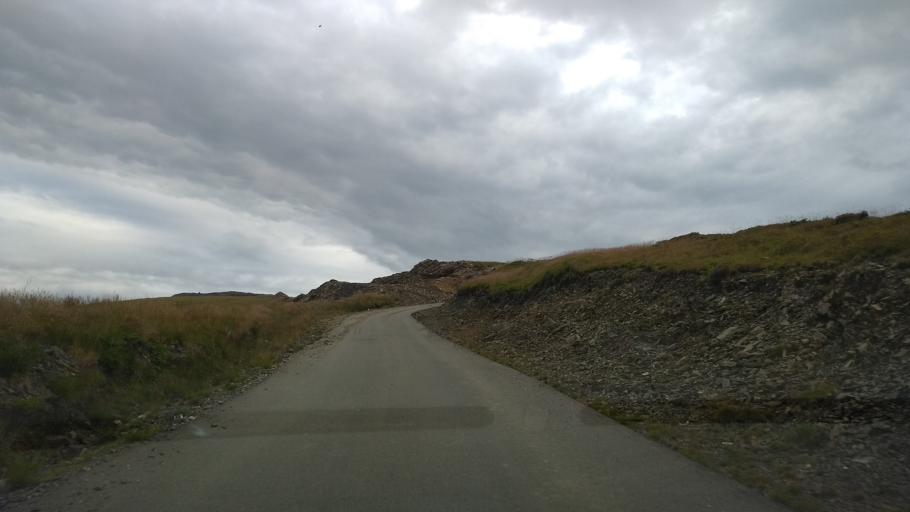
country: RO
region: Hunedoara
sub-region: Municipiul  Vulcan
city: Jiu-Paroseni
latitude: 45.3141
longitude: 23.3058
